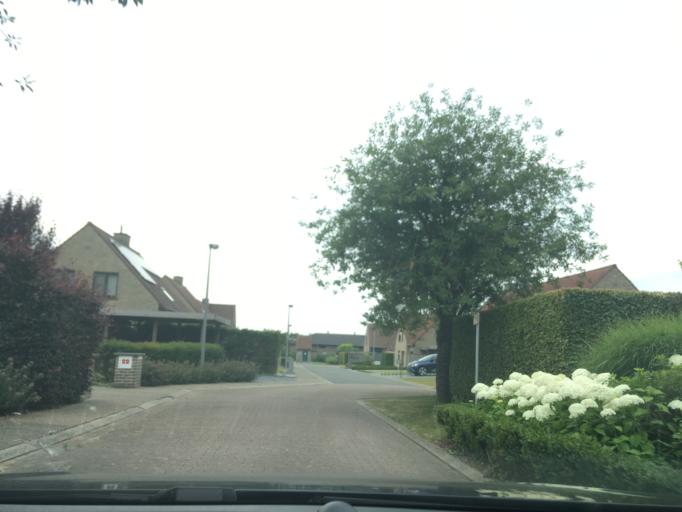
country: BE
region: Flanders
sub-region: Provincie West-Vlaanderen
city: Tielt
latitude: 50.9910
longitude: 3.3256
